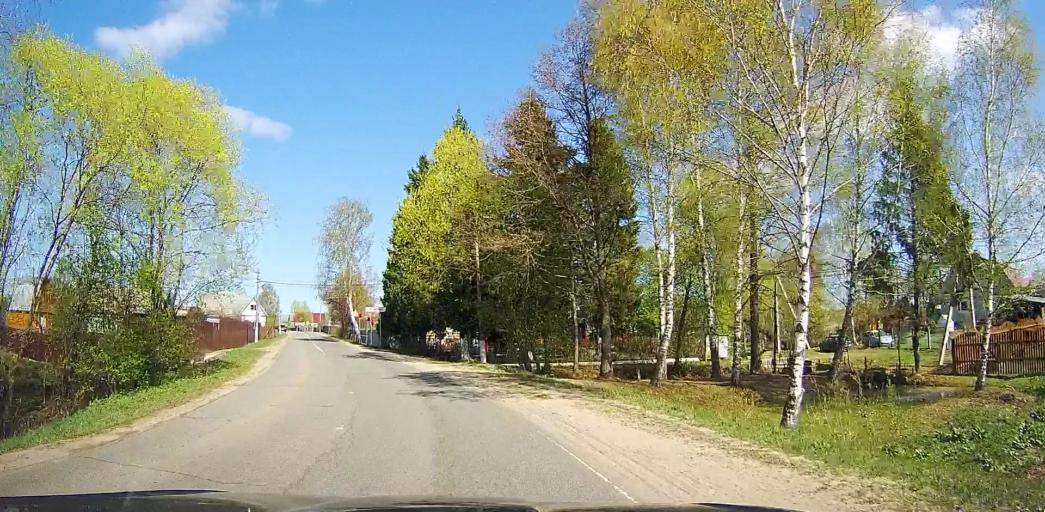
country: RU
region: Moskovskaya
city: Ramenskoye
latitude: 55.6139
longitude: 38.3037
